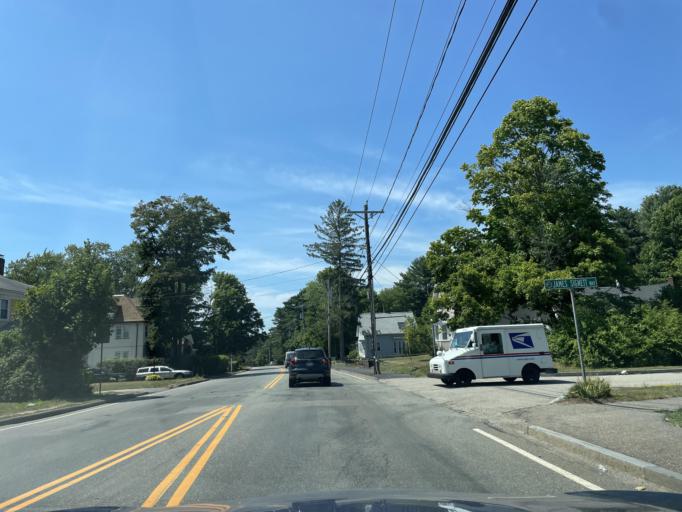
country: US
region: Massachusetts
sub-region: Norfolk County
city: Stoughton
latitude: 42.1338
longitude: -71.0927
